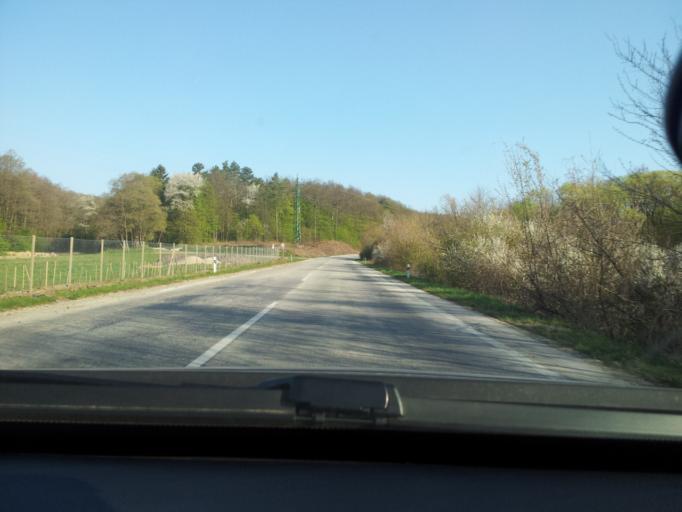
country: SK
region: Nitriansky
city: Zlate Moravce
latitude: 48.4511
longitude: 18.4124
